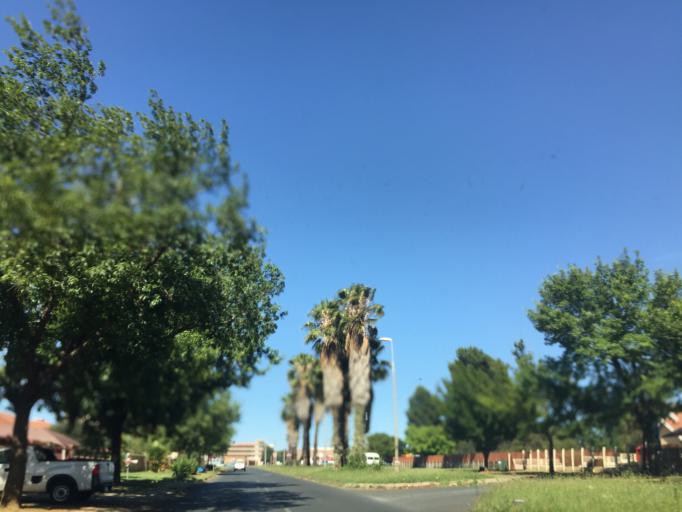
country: ZA
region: Gauteng
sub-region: Sedibeng District Municipality
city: Vanderbijlpark
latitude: -26.6974
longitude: 27.8424
